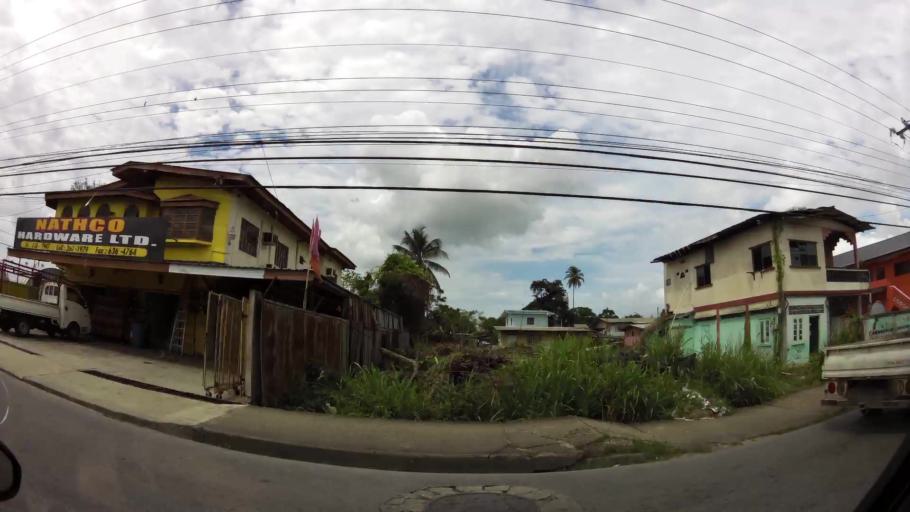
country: TT
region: Couva-Tabaquite-Talparo
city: Couva
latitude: 10.4078
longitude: -61.4716
